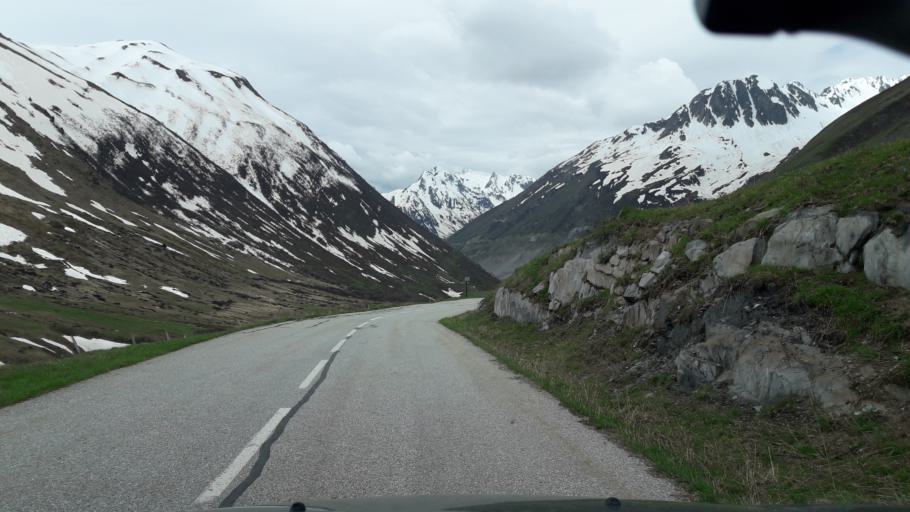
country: FR
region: Rhone-Alpes
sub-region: Departement de la Savoie
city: Saint-Etienne-de-Cuines
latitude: 45.2339
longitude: 6.1695
